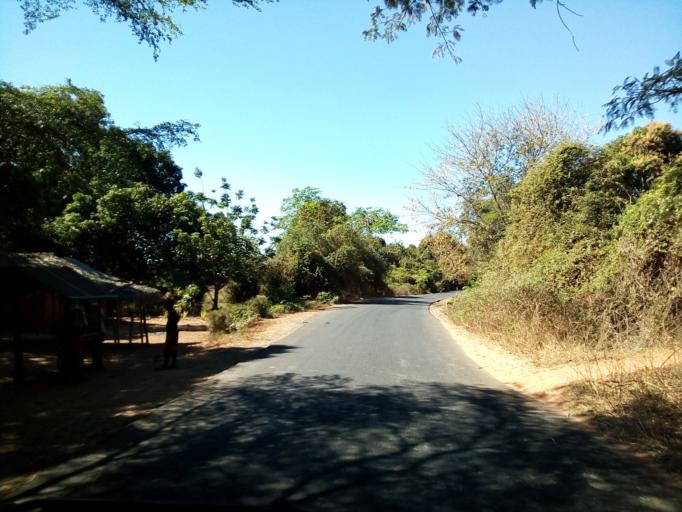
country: MG
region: Boeny
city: Ambato Boeny
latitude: -16.3237
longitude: 46.8313
